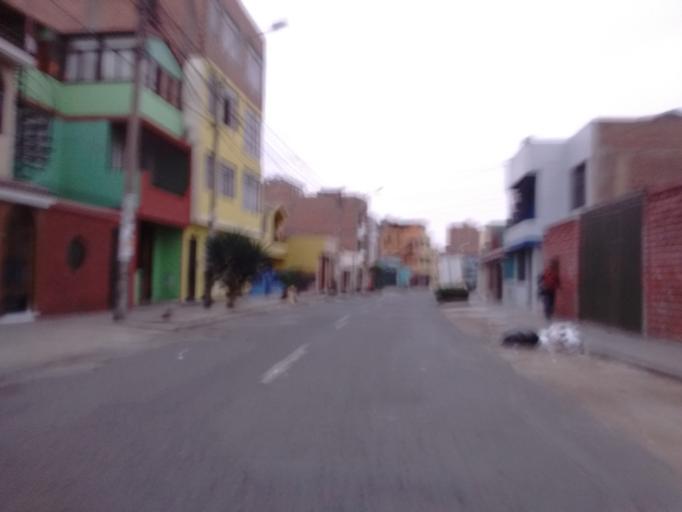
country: PE
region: Lima
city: Lima
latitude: -12.0530
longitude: -77.0723
